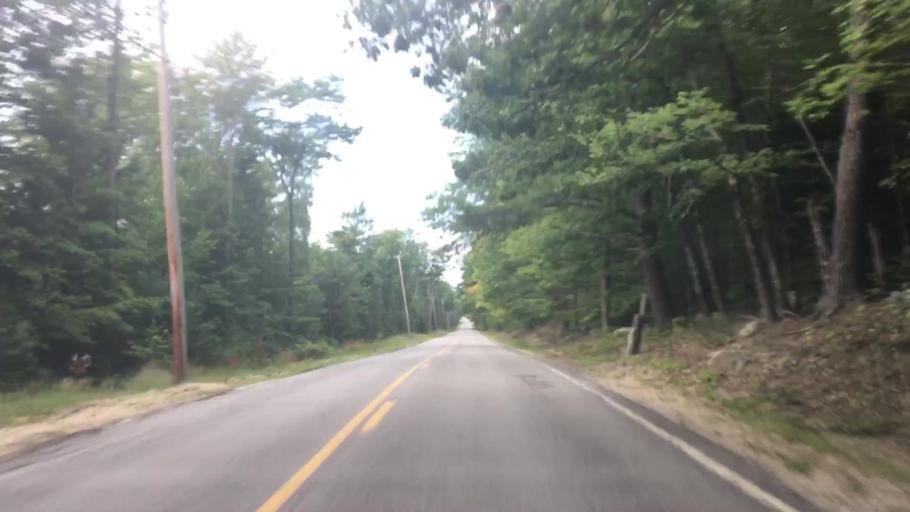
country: US
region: Maine
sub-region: Oxford County
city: Oxford
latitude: 44.0457
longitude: -70.5453
